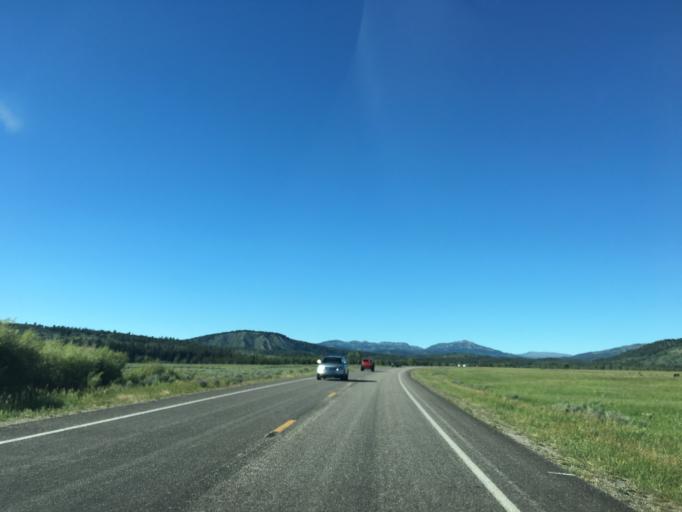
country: US
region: Wyoming
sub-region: Teton County
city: Jackson
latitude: 43.8153
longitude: -110.5258
